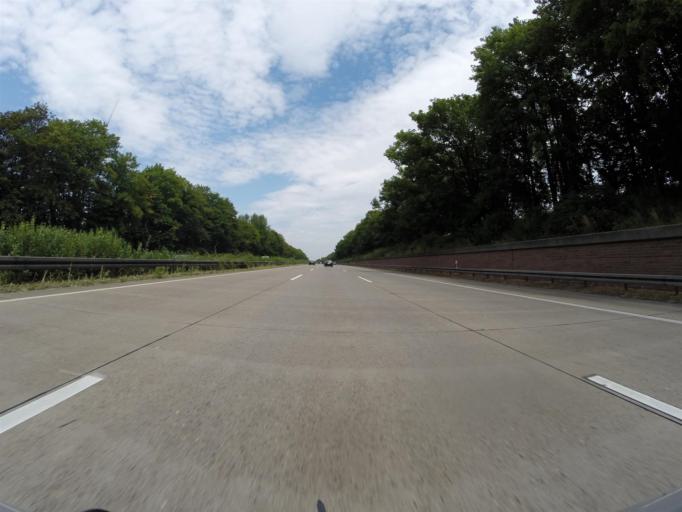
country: DE
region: Lower Saxony
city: Algermissen
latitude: 52.2660
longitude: 9.9157
